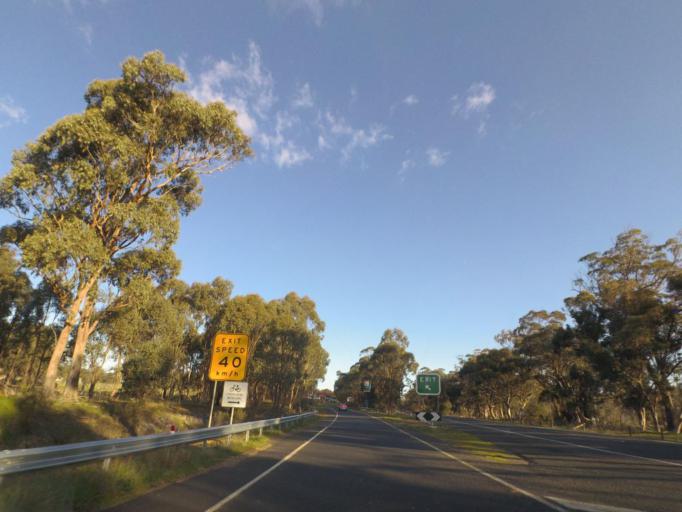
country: AU
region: Victoria
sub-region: Murrindindi
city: Kinglake West
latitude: -37.0609
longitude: 145.1012
